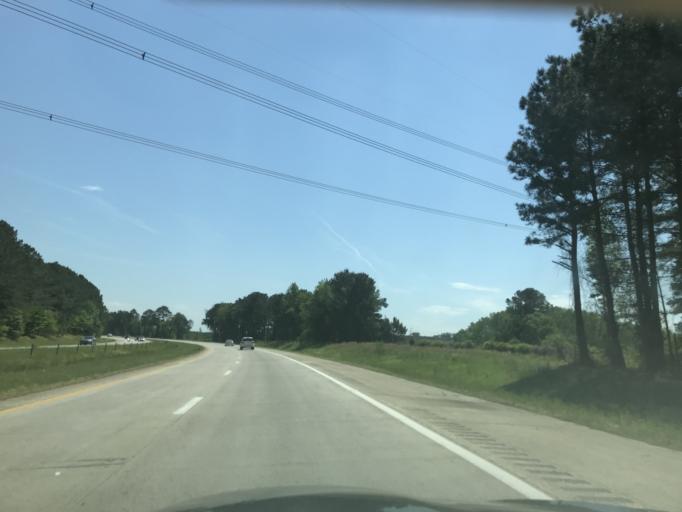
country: US
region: North Carolina
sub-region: Johnston County
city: Clayton
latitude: 35.5492
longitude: -78.5804
